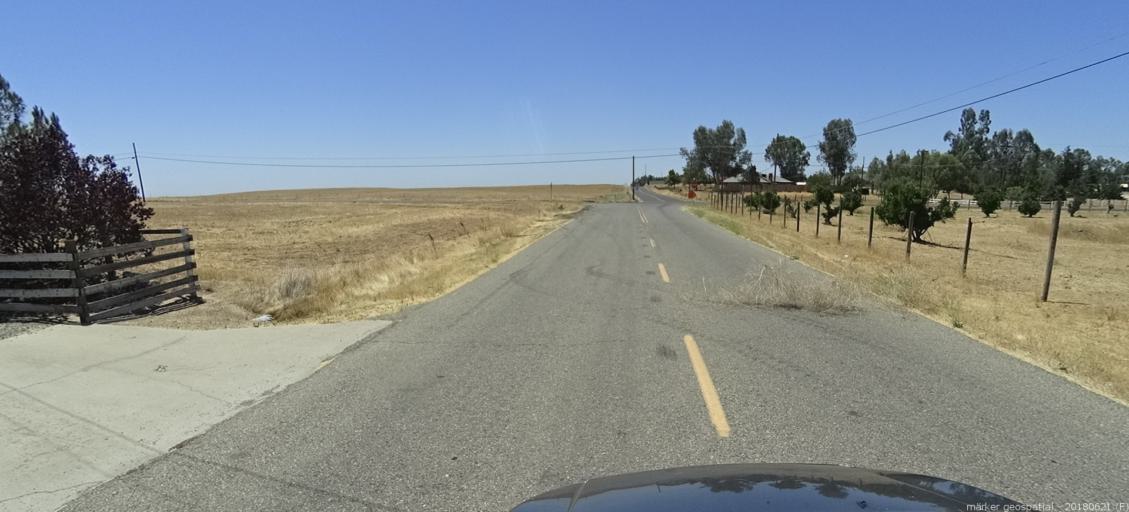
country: US
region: California
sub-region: Madera County
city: Bonadelle Ranchos-Madera Ranchos
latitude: 36.9820
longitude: -119.8758
